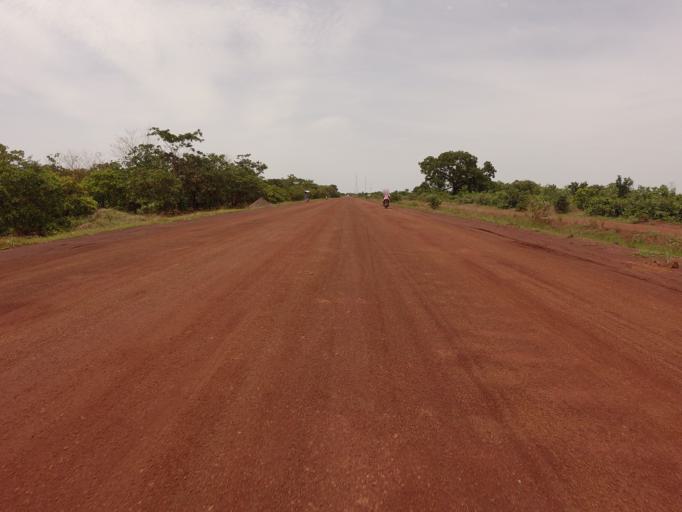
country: GH
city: Kpandae
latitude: 8.8810
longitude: 0.0343
